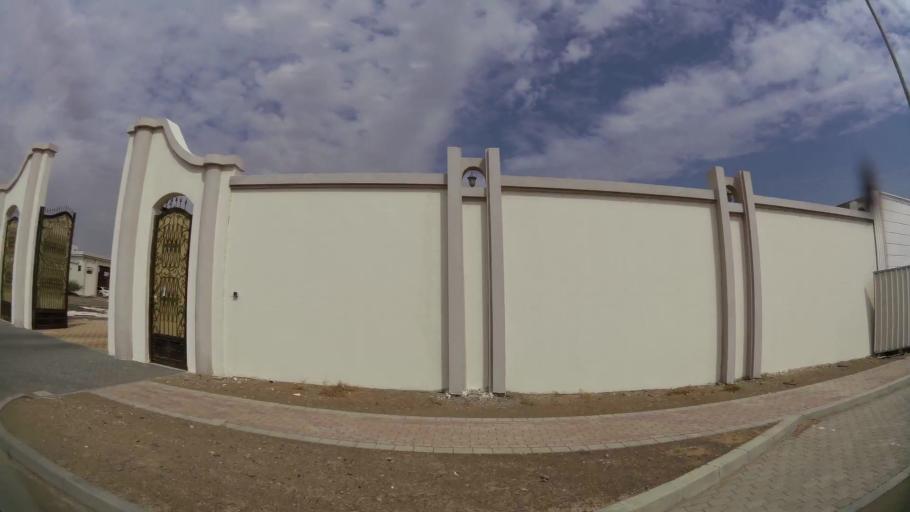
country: AE
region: Abu Dhabi
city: Al Ain
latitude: 24.1905
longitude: 55.8068
